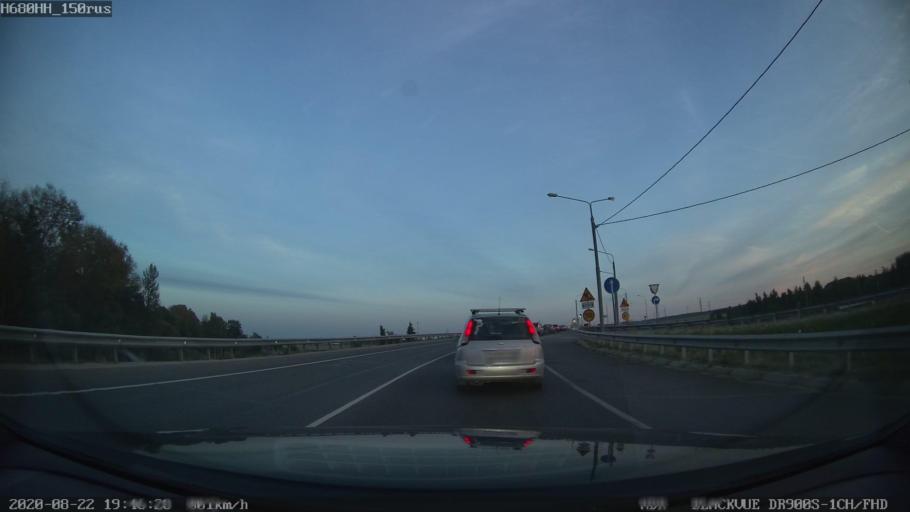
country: RU
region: Tverskaya
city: Emmaus
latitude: 56.7852
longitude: 36.0884
